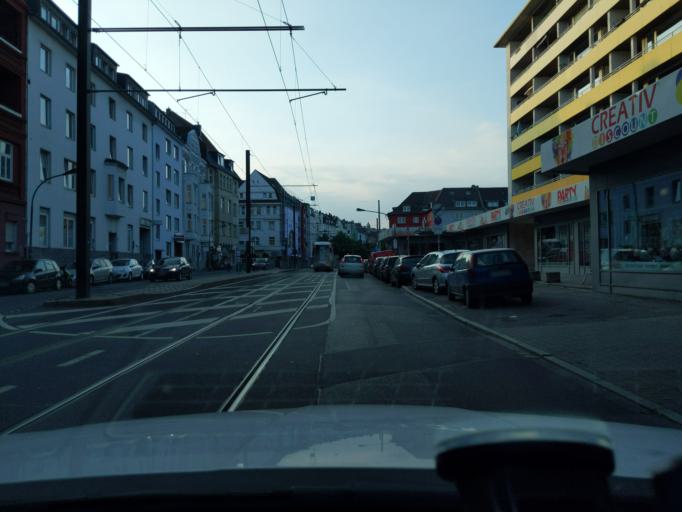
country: DE
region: North Rhine-Westphalia
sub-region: Regierungsbezirk Dusseldorf
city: Dusseldorf
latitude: 51.2016
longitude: 6.7811
